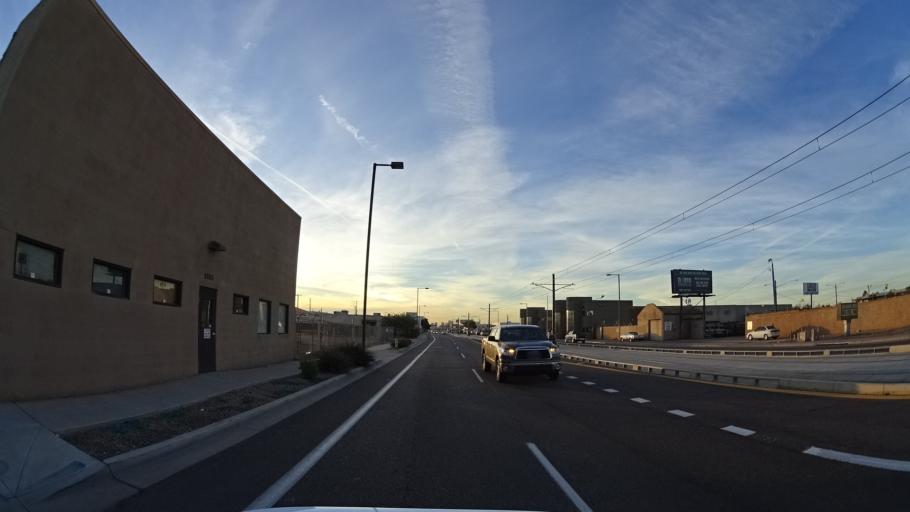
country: US
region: Arizona
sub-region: Maricopa County
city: Phoenix
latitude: 33.4481
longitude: -112.0086
